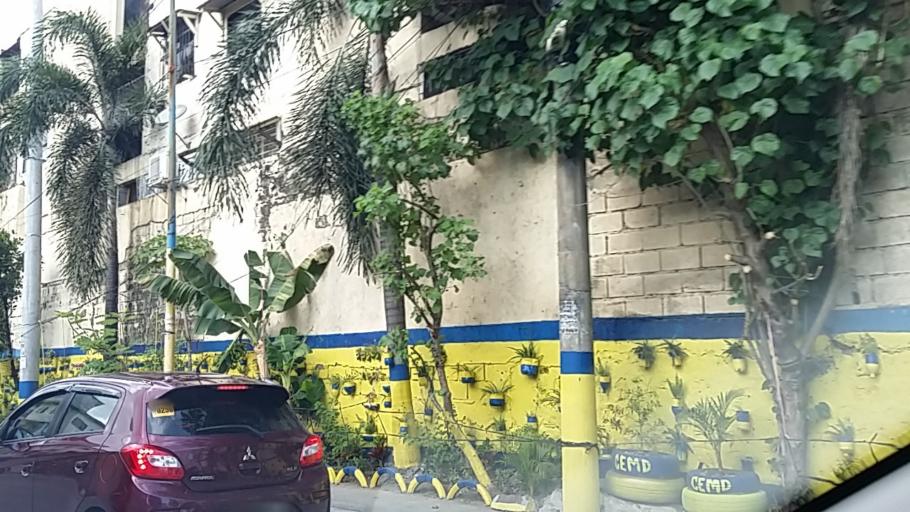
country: PH
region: Metro Manila
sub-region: Mandaluyong
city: Mandaluyong City
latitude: 14.5800
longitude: 121.0454
